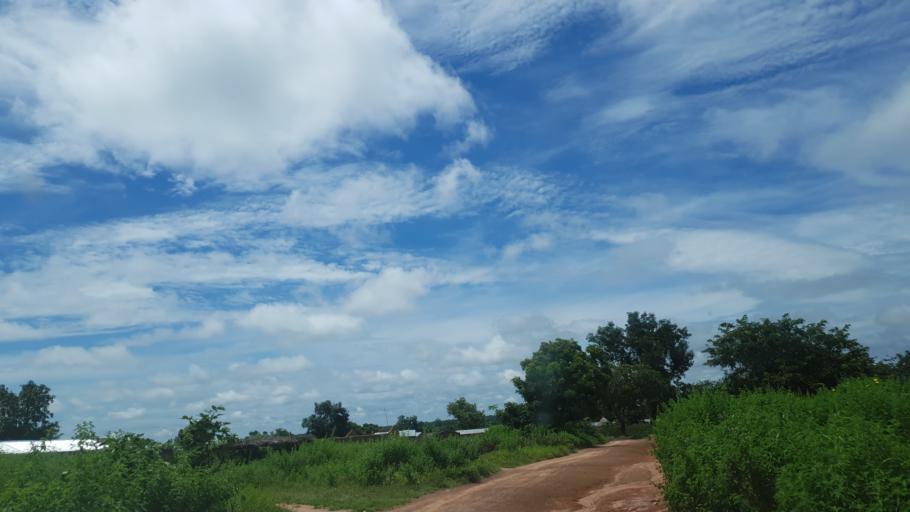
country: CI
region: Savanes
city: Tengrela
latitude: 10.3635
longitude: -6.9193
